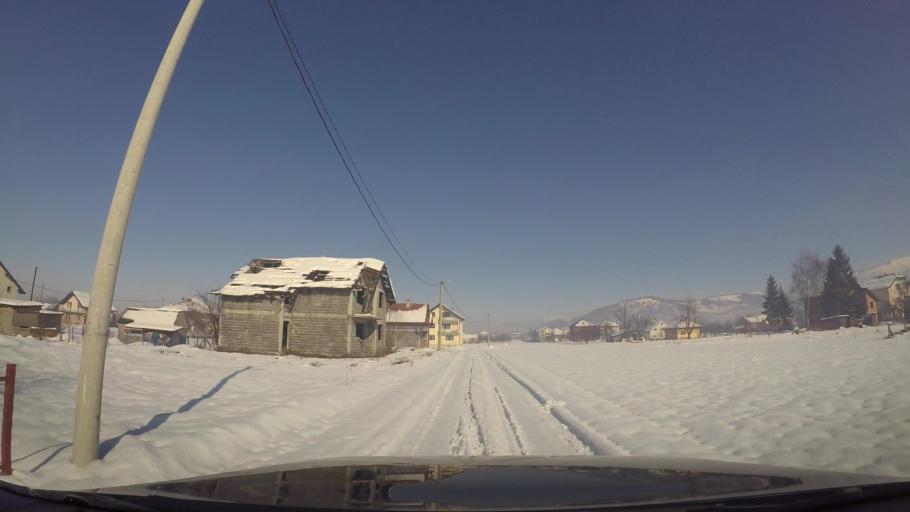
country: BA
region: Federation of Bosnia and Herzegovina
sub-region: Kanton Sarajevo
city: Sarajevo
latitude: 43.7934
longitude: 18.3401
